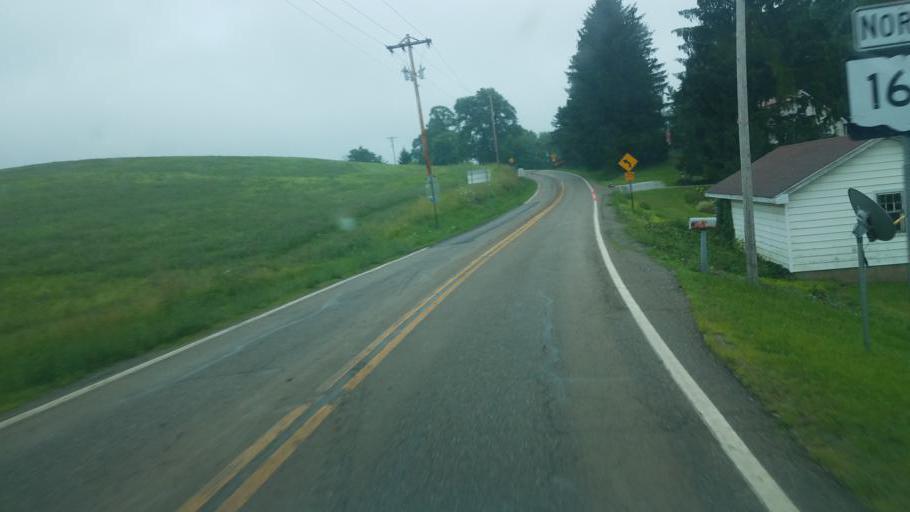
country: US
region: Ohio
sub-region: Carroll County
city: Carrollton
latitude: 40.4647
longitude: -81.0939
